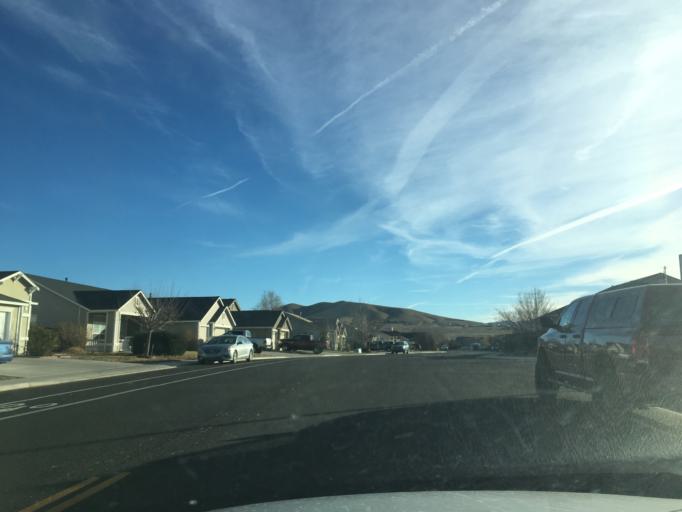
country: US
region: Nevada
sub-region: Lyon County
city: Fernley
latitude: 39.5929
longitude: -119.2302
